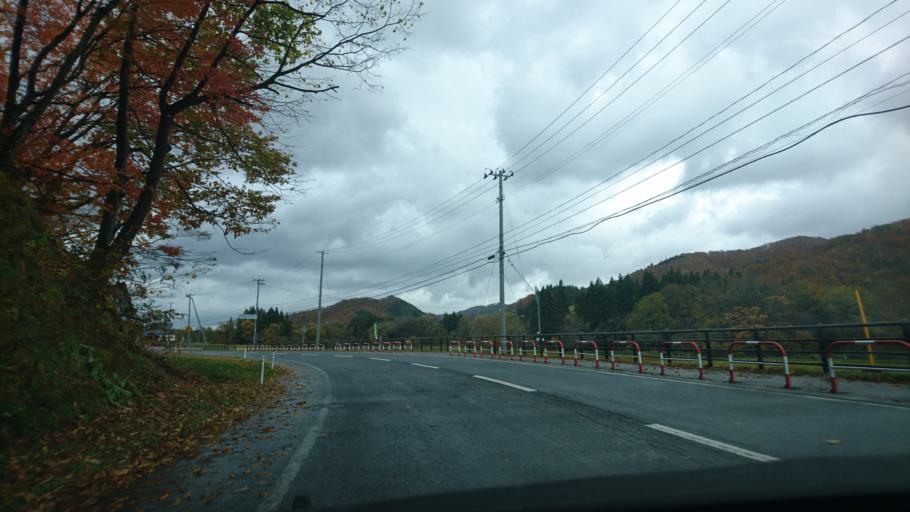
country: JP
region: Iwate
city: Shizukuishi
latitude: 39.5089
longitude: 140.8277
